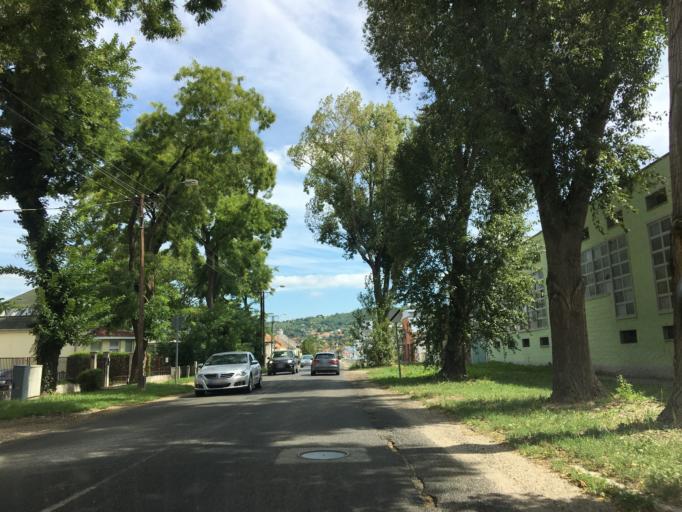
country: HU
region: Komarom-Esztergom
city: Esztergom
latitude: 47.7801
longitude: 18.7331
